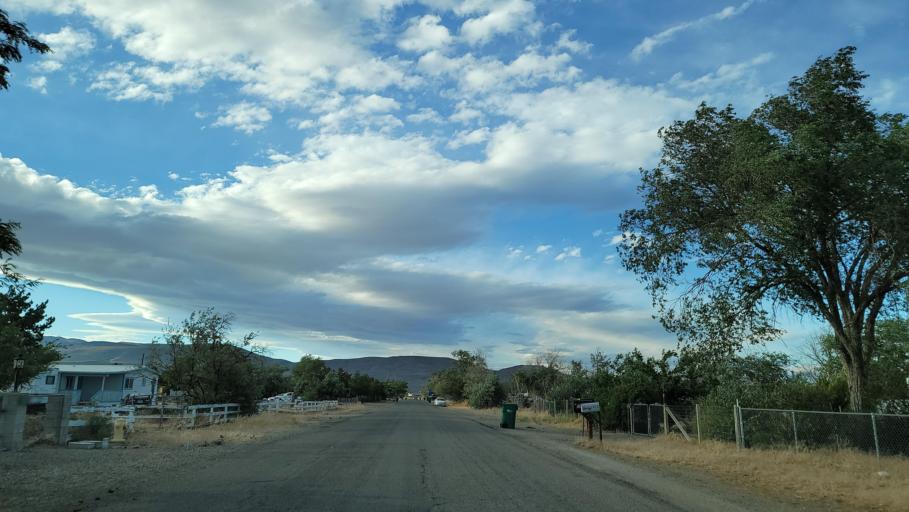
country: US
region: Nevada
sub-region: Lyon County
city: Silver Springs
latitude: 39.3931
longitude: -119.2374
